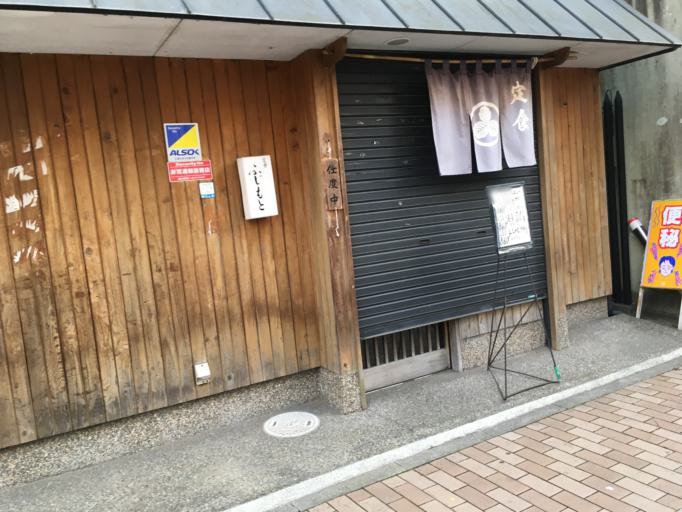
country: JP
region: Tochigi
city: Utsunomiya-shi
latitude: 36.5598
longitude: 139.8875
